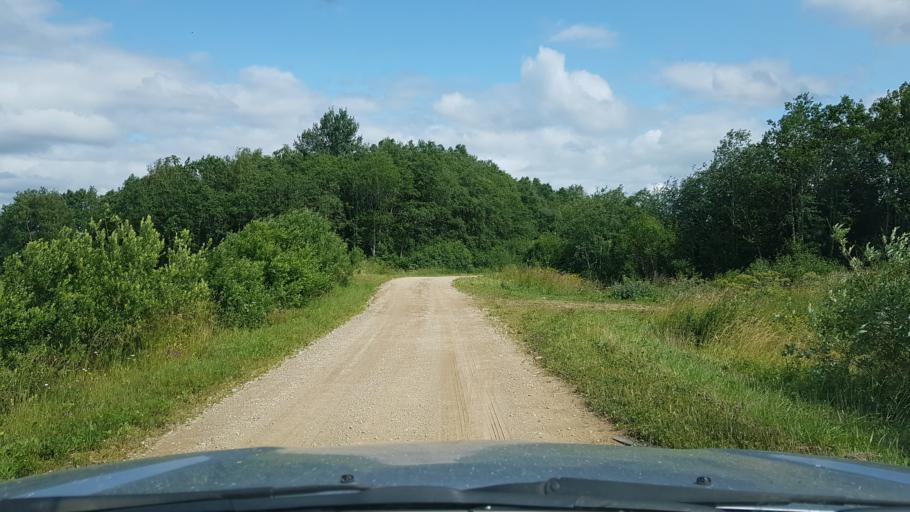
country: EE
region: Ida-Virumaa
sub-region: Narva-Joesuu linn
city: Narva-Joesuu
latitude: 59.3703
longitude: 27.9231
